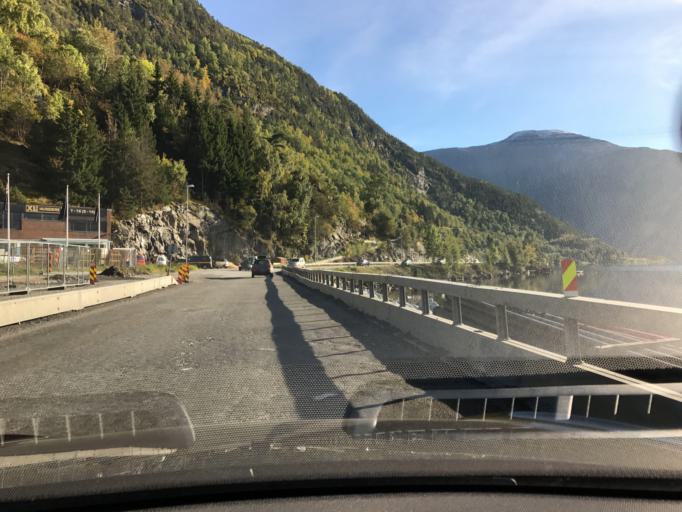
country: NO
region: Sogn og Fjordane
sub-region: Sogndal
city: Sogndalsfjora
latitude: 61.2293
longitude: 7.1246
